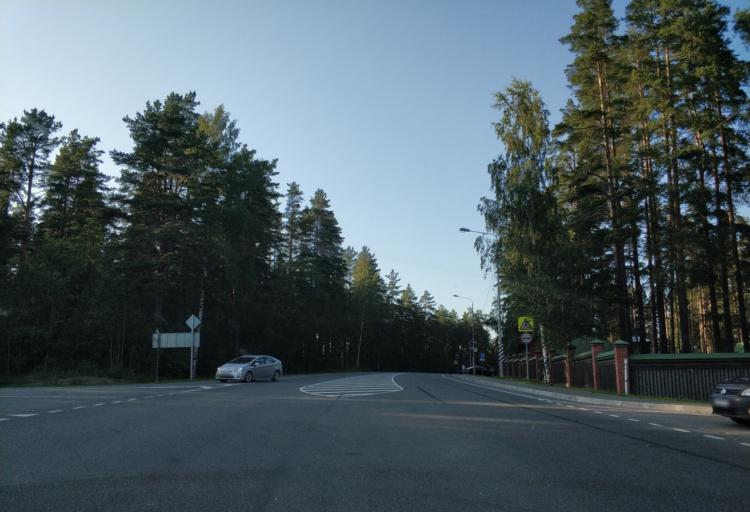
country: RU
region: Leningrad
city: Sapernoye
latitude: 60.7059
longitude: 29.9683
